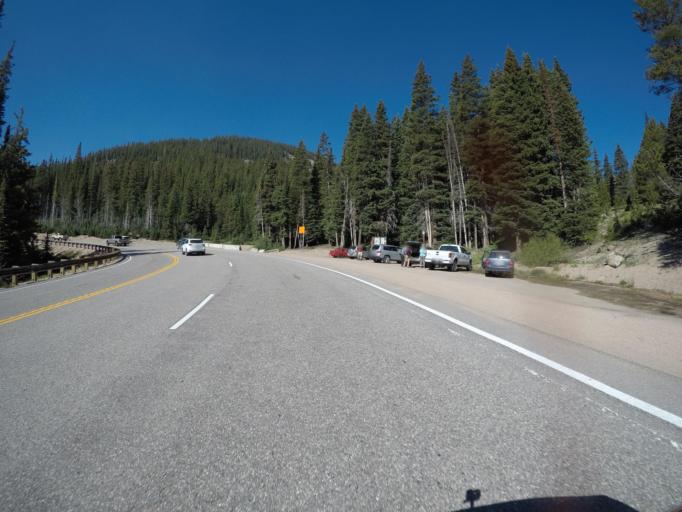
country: US
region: Colorado
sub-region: Grand County
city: Fraser
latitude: 39.8228
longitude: -105.7693
